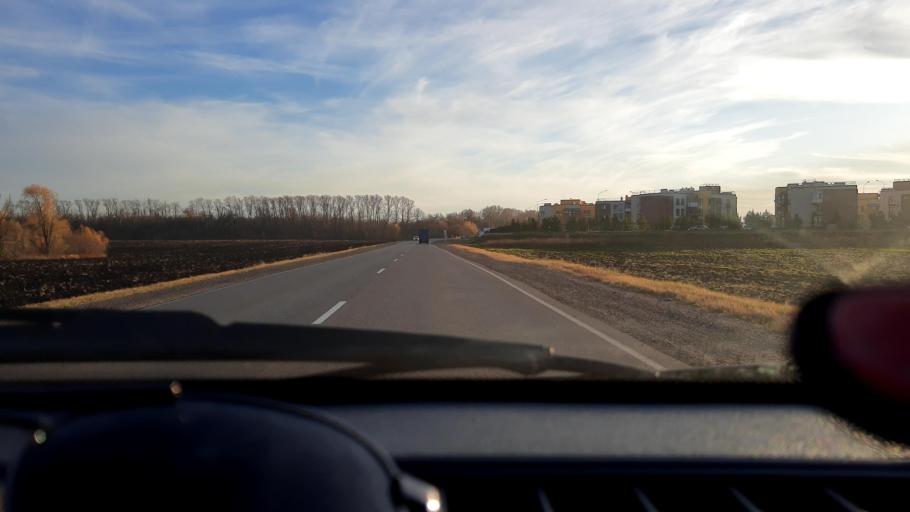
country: RU
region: Bashkortostan
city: Ufa
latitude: 54.8001
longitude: 55.9629
